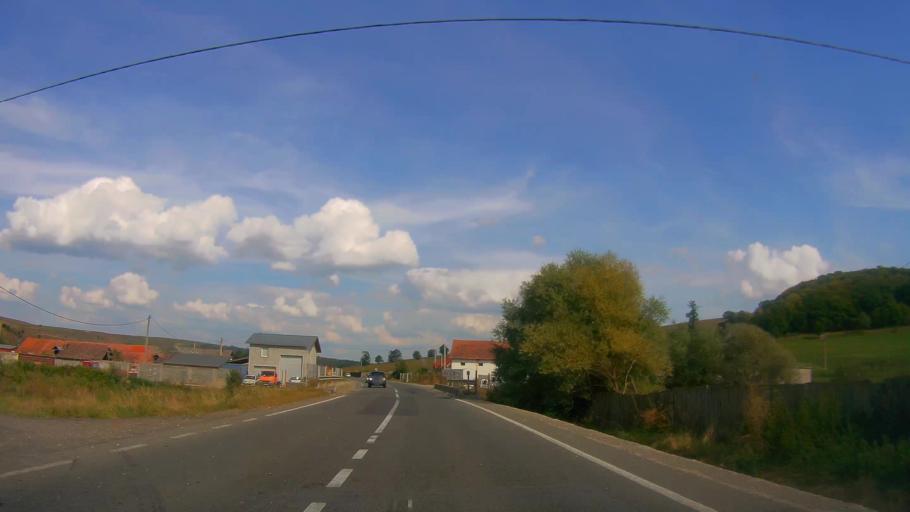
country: RO
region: Brasov
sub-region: Oras Rupea
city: Rupea
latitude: 46.0350
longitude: 25.2326
